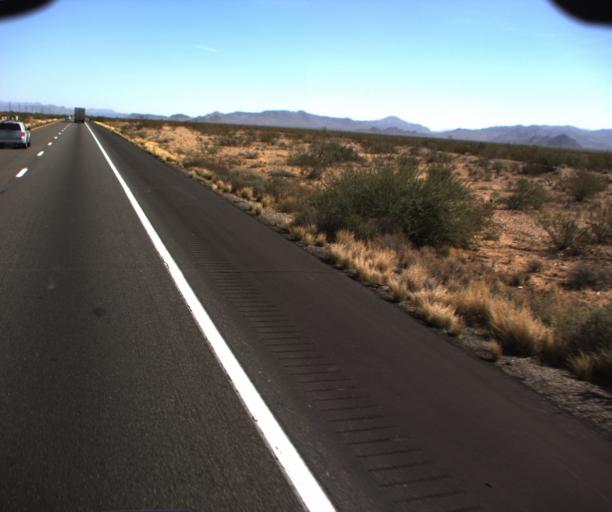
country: US
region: Arizona
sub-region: Mohave County
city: Kingman
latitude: 34.9857
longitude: -114.1390
